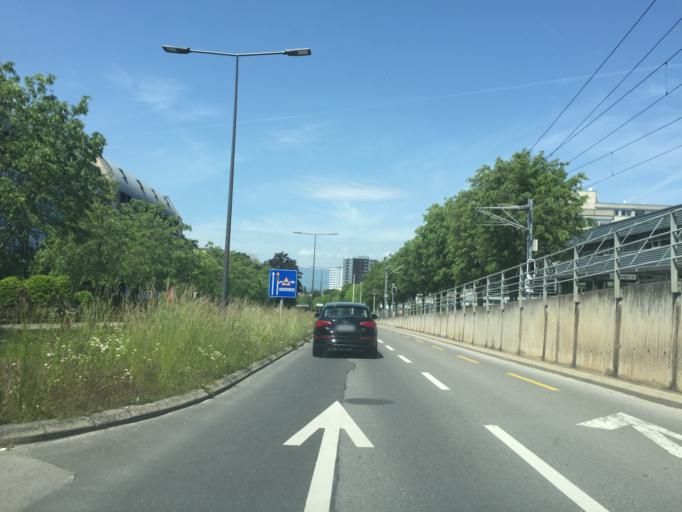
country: CH
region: Vaud
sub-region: Lausanne District
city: Blecherette
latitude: 46.5220
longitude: 6.6127
